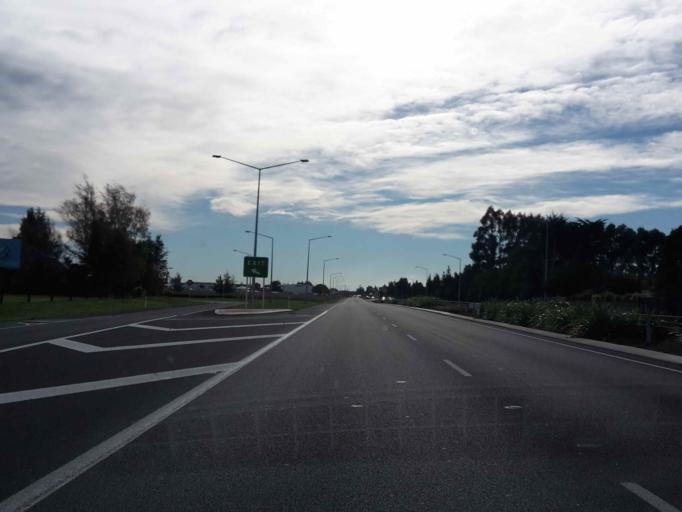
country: NZ
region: Canterbury
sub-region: Selwyn District
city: Prebbleton
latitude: -43.5030
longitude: 172.5440
